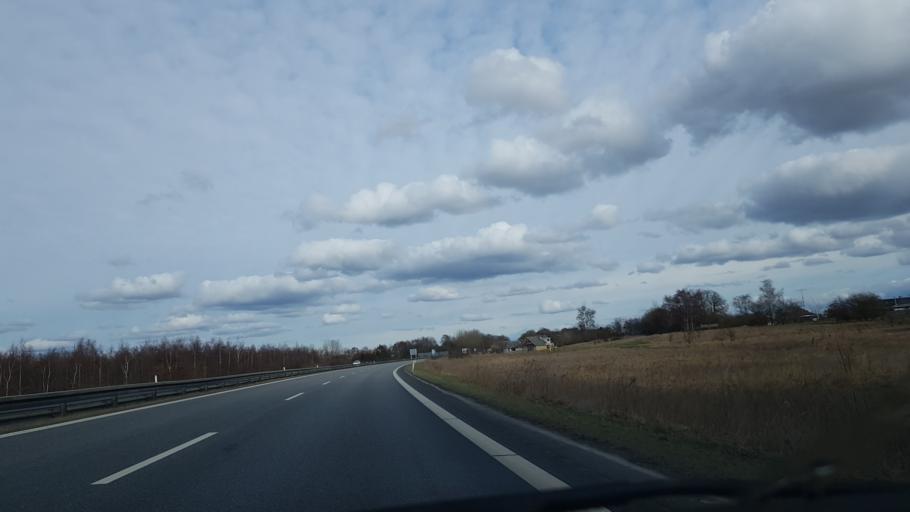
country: DK
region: Zealand
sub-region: Slagelse Kommune
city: Korsor
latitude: 55.3591
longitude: 11.1624
